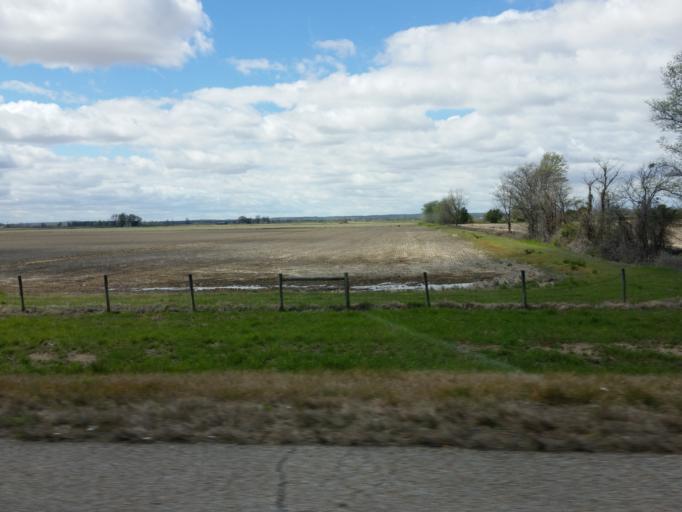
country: US
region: Arkansas
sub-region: Craighead County
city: Bay
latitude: 35.7376
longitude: -90.5802
